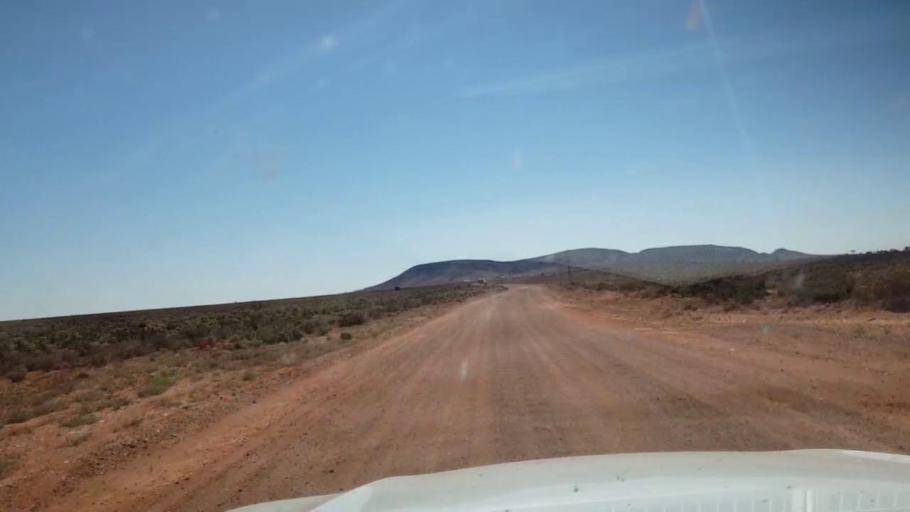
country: AU
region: South Australia
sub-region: Whyalla
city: Whyalla
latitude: -32.7143
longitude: 137.1424
